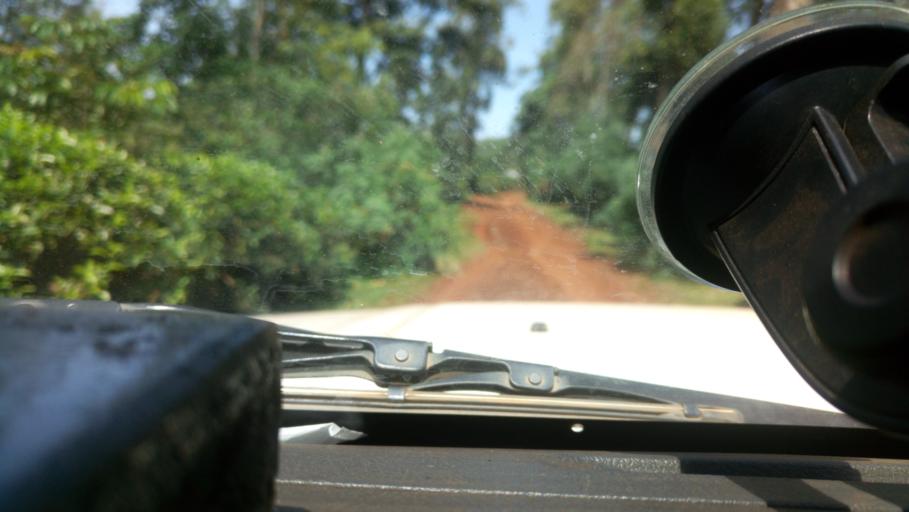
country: KE
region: Kisii
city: Ogembo
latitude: -0.8563
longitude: 34.7036
